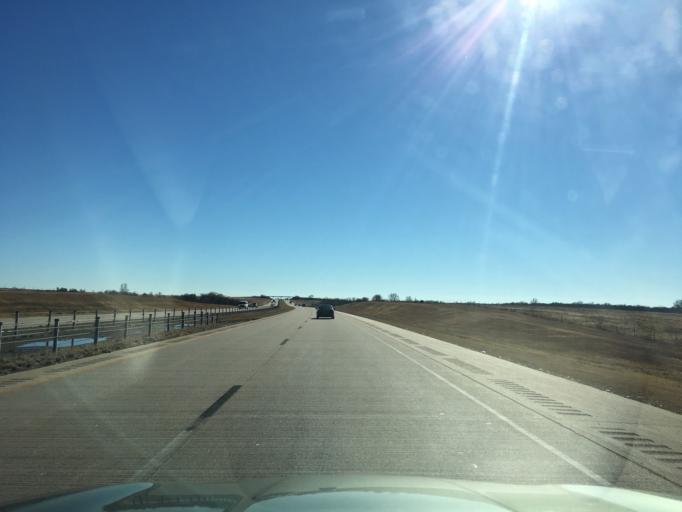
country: US
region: Oklahoma
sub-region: Kay County
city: Tonkawa
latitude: 36.5033
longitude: -97.3355
